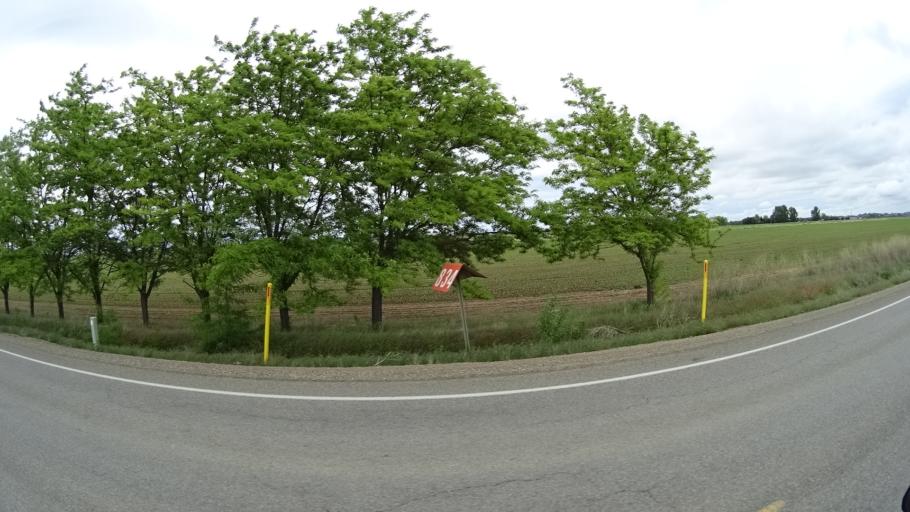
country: US
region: Idaho
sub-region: Ada County
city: Star
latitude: 43.6378
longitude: -116.4936
